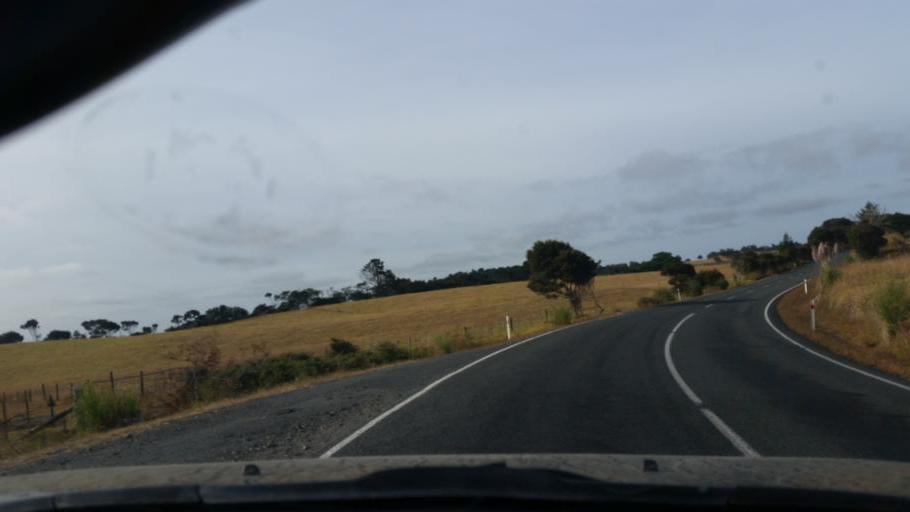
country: NZ
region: Northland
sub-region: Kaipara District
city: Dargaville
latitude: -36.1968
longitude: 174.0514
